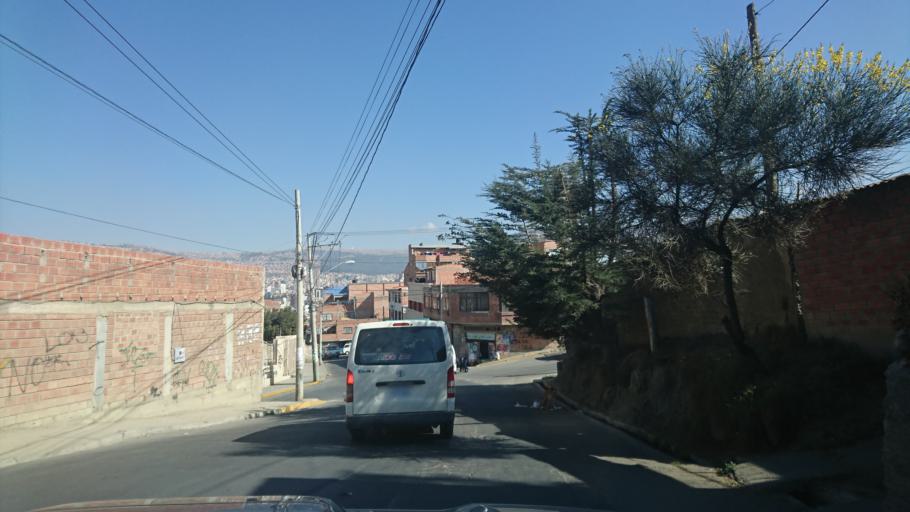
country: BO
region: La Paz
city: La Paz
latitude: -16.5097
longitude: -68.1084
